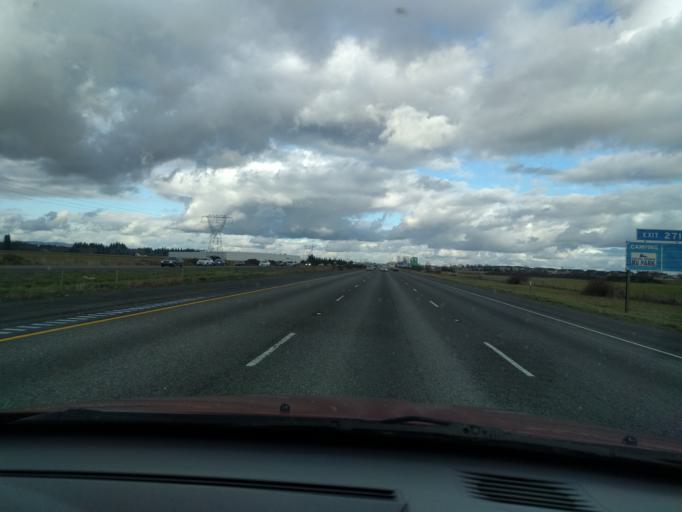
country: US
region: Oregon
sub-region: Marion County
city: Gervais
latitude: 45.1360
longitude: -122.8960
